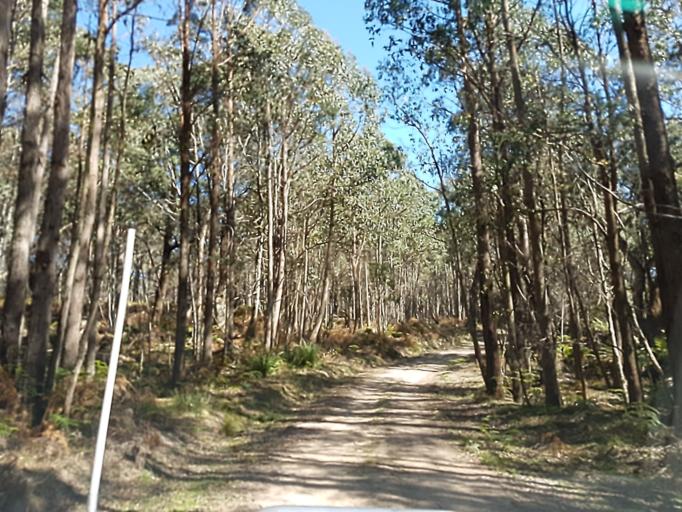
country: AU
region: Victoria
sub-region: East Gippsland
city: Lakes Entrance
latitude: -37.2300
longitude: 148.2872
